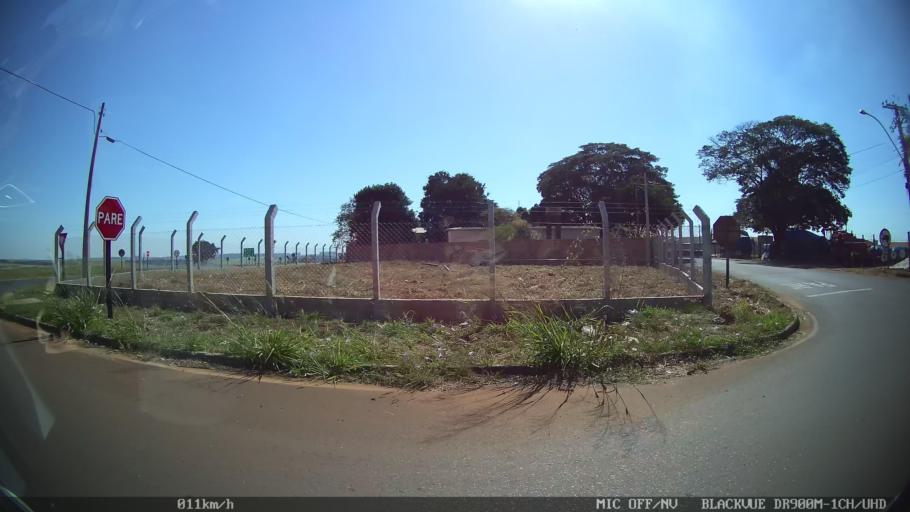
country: BR
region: Sao Paulo
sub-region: Batatais
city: Batatais
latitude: -20.8756
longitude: -47.5994
